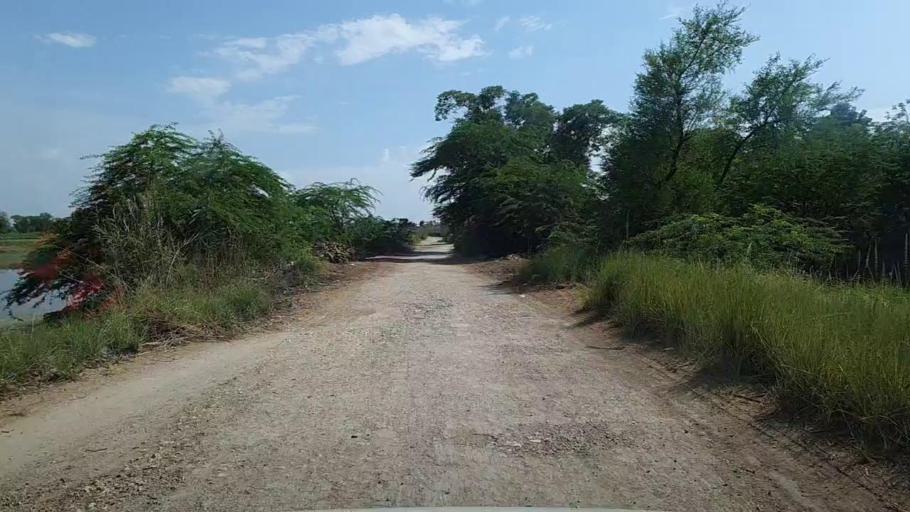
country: PK
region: Sindh
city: Bhiria
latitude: 26.9021
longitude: 68.2269
